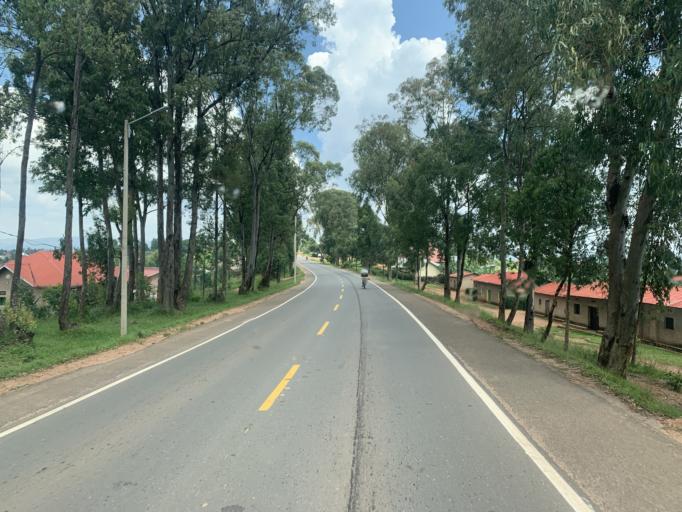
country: RW
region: Kigali
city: Kigali
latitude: -1.9985
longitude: 29.9084
